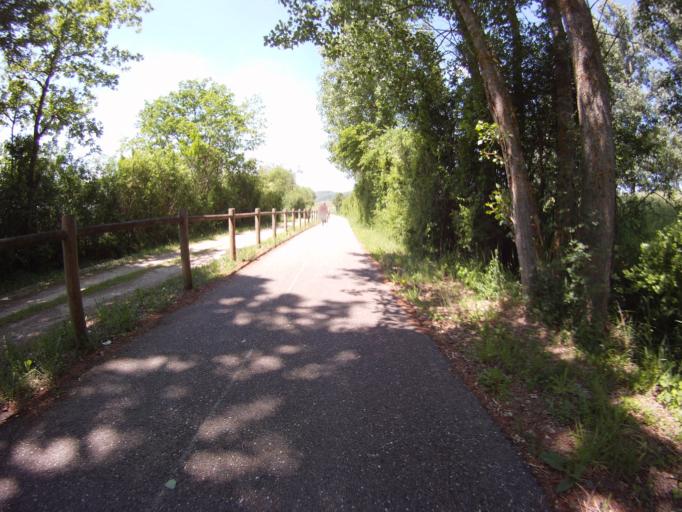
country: FR
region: Lorraine
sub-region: Departement de Meurthe-et-Moselle
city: Champenoux
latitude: 48.7411
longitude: 6.3050
